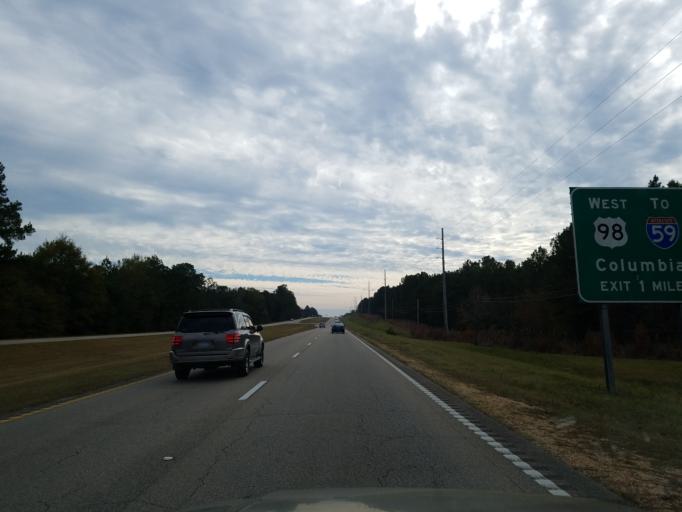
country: US
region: Mississippi
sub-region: Forrest County
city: Hattiesburg
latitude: 31.2614
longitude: -89.2829
